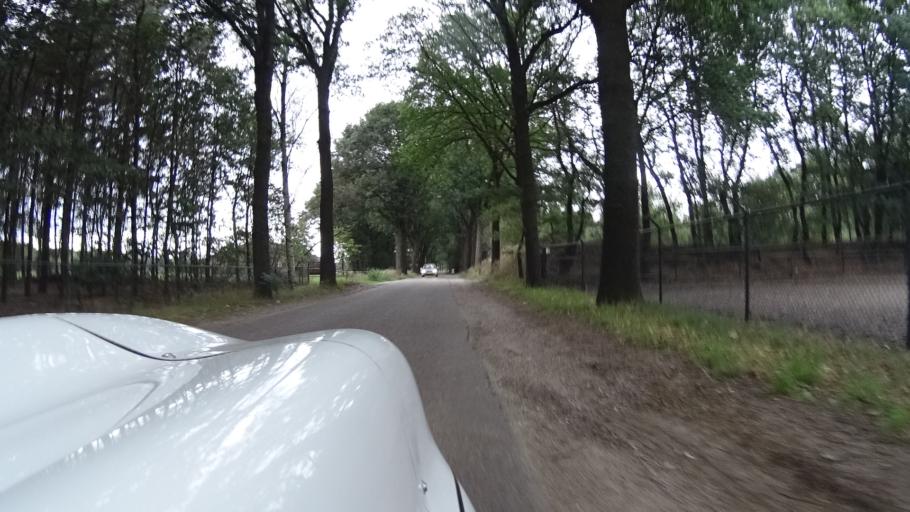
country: NL
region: North Brabant
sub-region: Gemeente Veghel
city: Mariaheide
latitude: 51.6608
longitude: 5.5612
